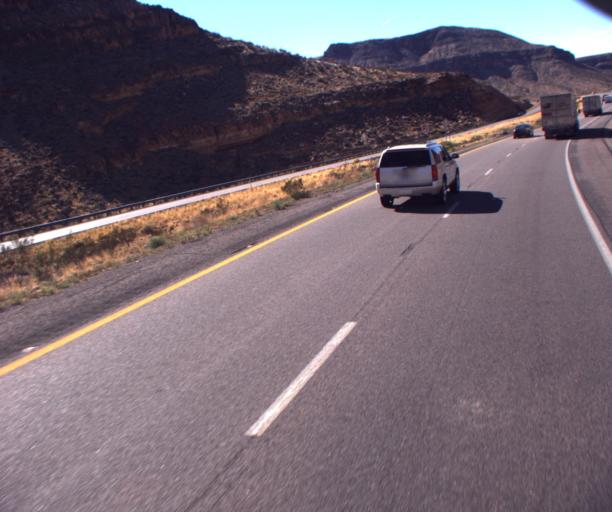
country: US
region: Utah
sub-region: Washington County
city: Saint George
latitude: 36.9765
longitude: -113.6774
